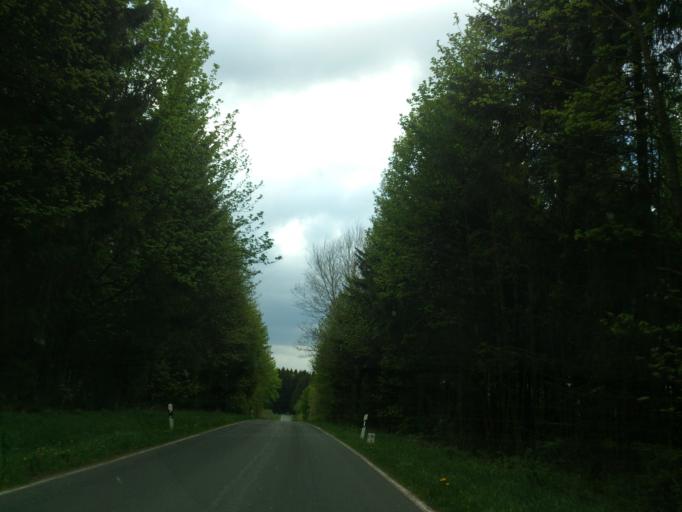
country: DE
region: North Rhine-Westphalia
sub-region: Regierungsbezirk Detmold
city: Willebadessen
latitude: 51.5964
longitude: 8.9921
